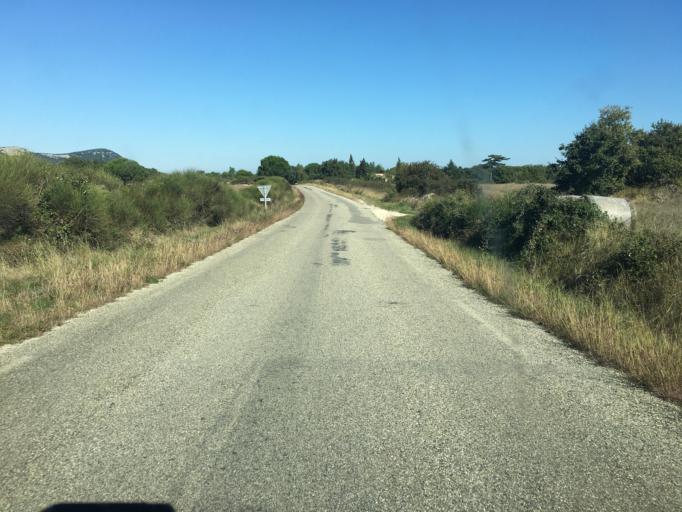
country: FR
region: Languedoc-Roussillon
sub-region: Departement du Gard
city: Barjac
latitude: 44.1700
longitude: 4.3201
